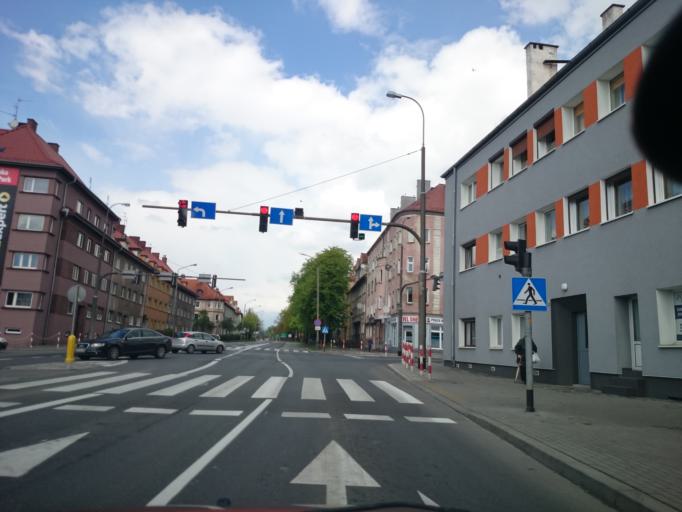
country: PL
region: Opole Voivodeship
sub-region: Powiat opolski
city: Opole
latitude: 50.6637
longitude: 17.9424
